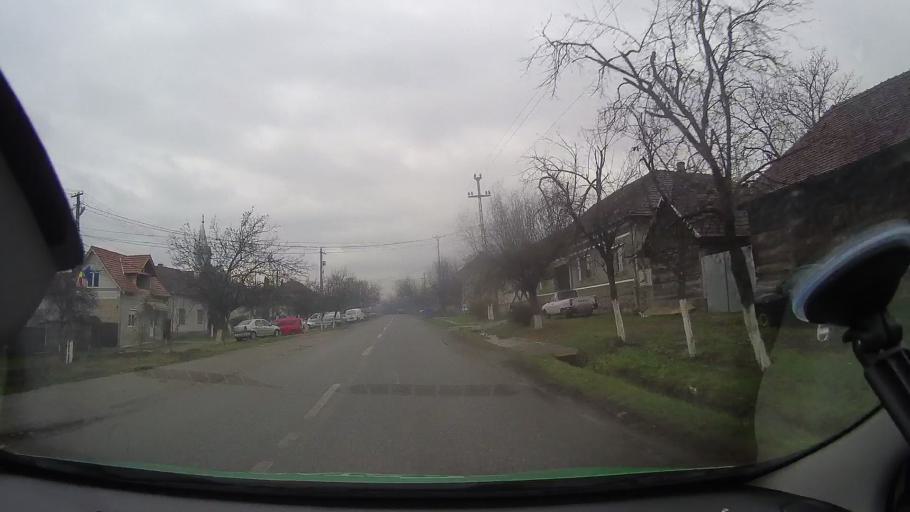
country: RO
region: Arad
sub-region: Comuna Gurahont
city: Gurahont
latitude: 46.2699
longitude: 22.3440
